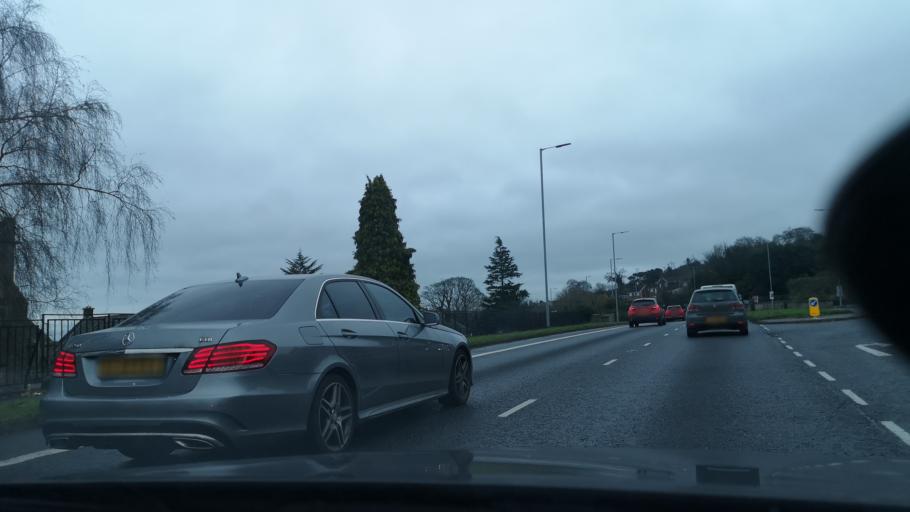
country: GB
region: Northern Ireland
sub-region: Castlereagh District
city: Castlereagh
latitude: 54.5701
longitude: -5.8909
